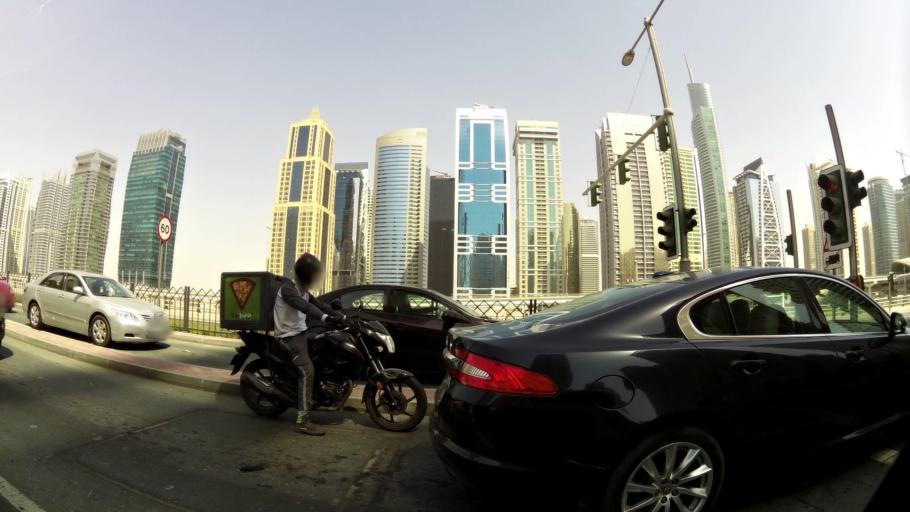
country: AE
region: Dubai
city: Dubai
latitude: 25.0738
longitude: 55.1393
